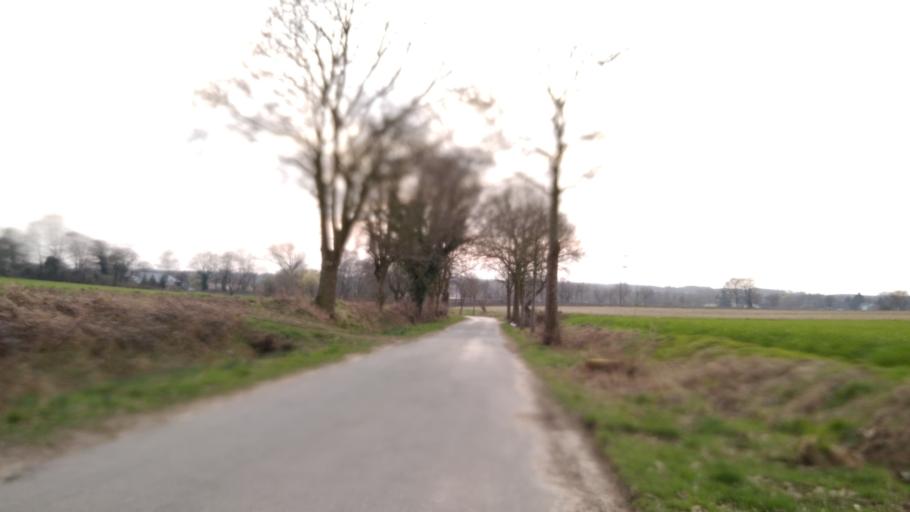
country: DE
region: North Rhine-Westphalia
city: Herten
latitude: 51.5981
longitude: 7.1199
